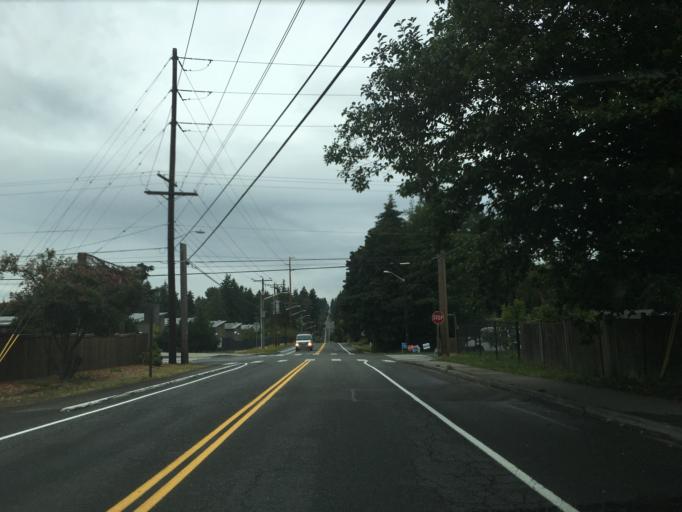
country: US
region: Washington
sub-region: King County
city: Inglewood-Finn Hill
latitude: 47.7184
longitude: -122.2294
